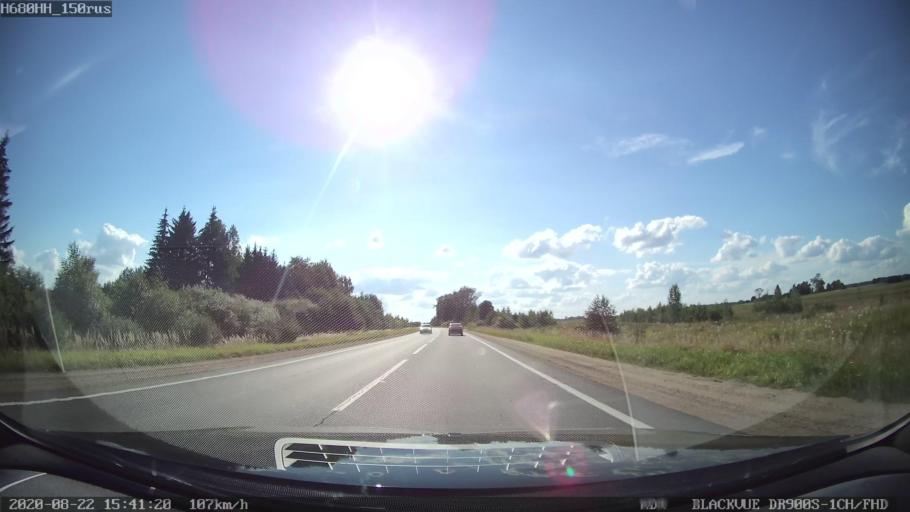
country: RU
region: Tverskaya
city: Bezhetsk
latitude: 57.7492
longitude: 36.5686
